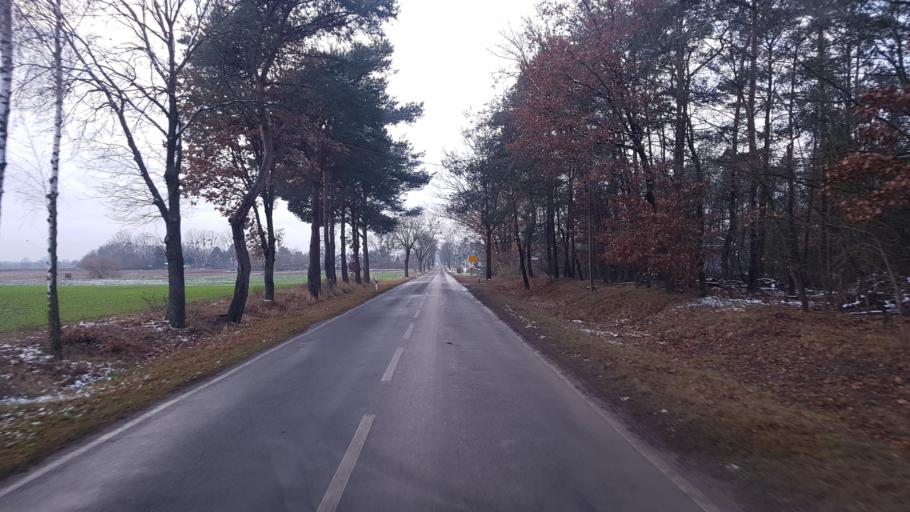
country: DE
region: Brandenburg
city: Rehfelde
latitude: 52.5099
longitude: 13.8720
